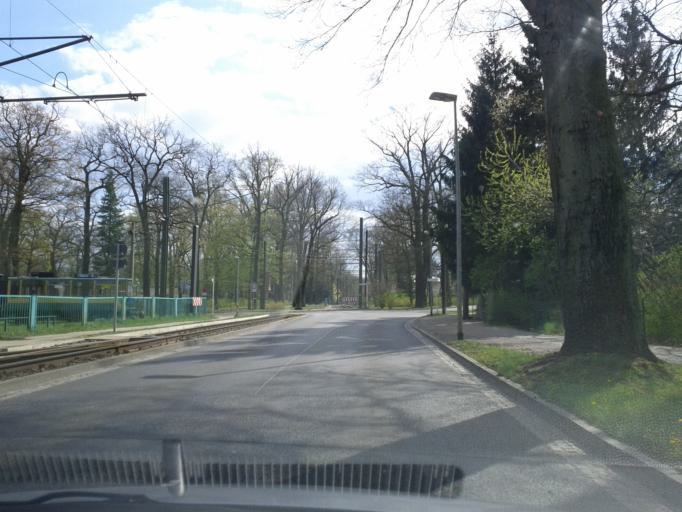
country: DE
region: Brandenburg
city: Schoneiche
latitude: 52.4761
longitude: 13.6932
